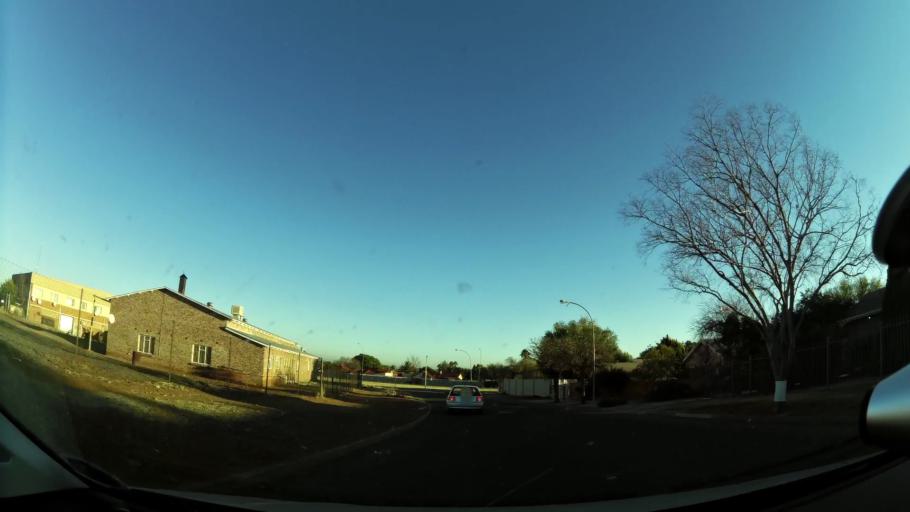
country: ZA
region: Northern Cape
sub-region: Frances Baard District Municipality
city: Kimberley
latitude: -28.7544
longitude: 24.7315
